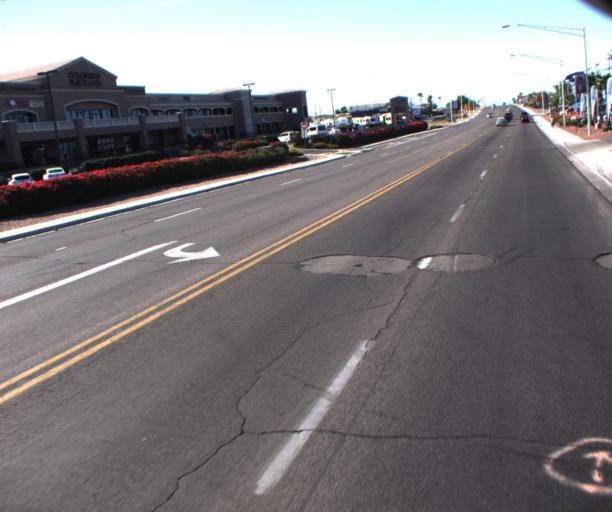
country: US
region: Arizona
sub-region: Mohave County
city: Bullhead City
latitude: 35.0930
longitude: -114.5981
